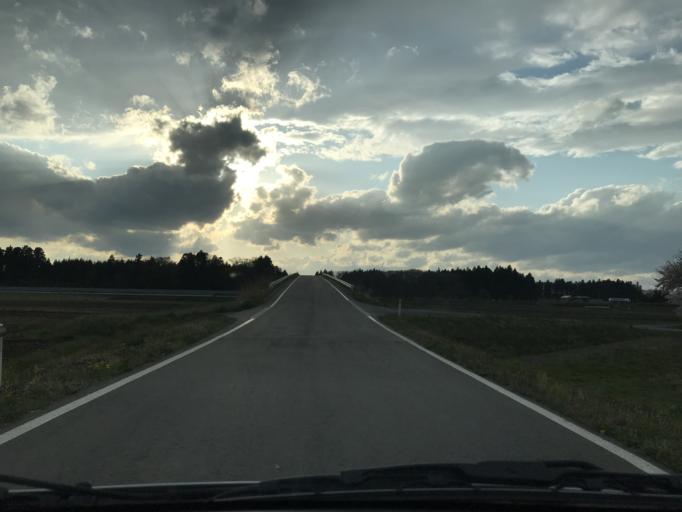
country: JP
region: Iwate
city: Mizusawa
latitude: 39.1000
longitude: 141.1193
